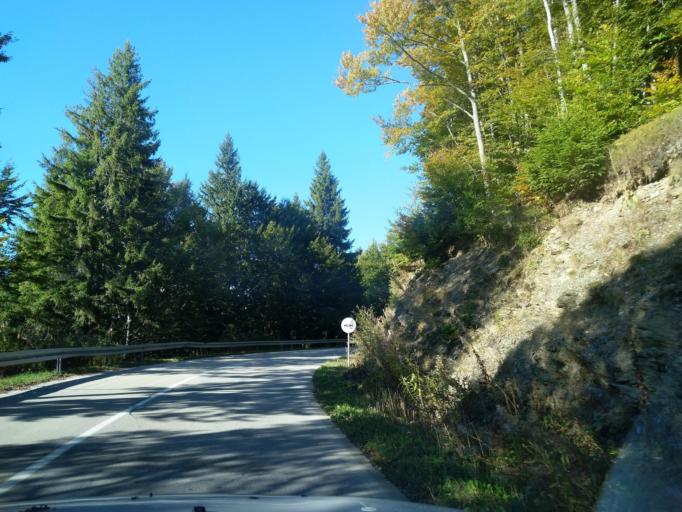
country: RS
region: Central Serbia
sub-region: Moravicki Okrug
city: Ivanjica
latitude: 43.4154
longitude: 20.2659
